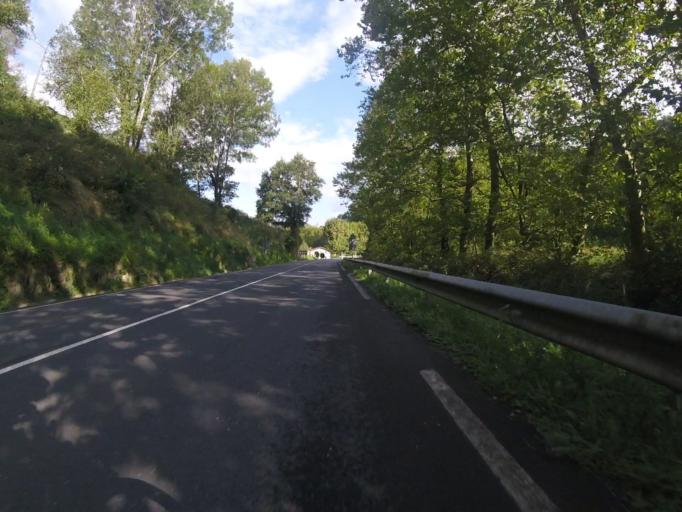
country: ES
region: Basque Country
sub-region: Provincia de Guipuzcoa
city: Orendain
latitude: 43.0743
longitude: -2.0870
